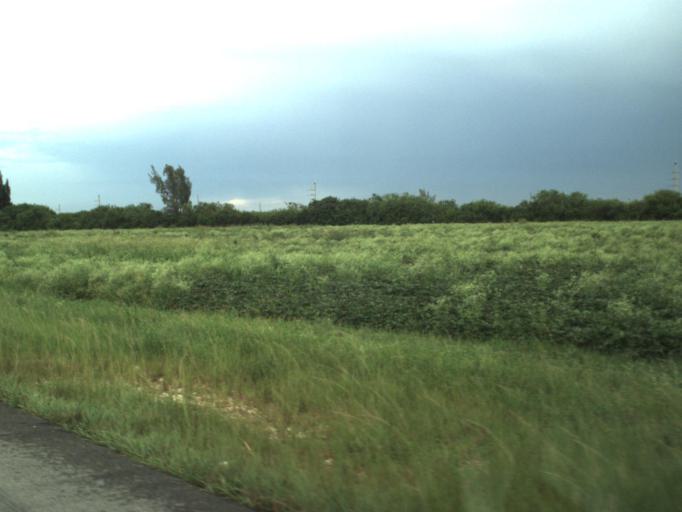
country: US
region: Florida
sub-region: Miami-Dade County
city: The Hammocks
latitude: 25.6761
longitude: -80.4810
